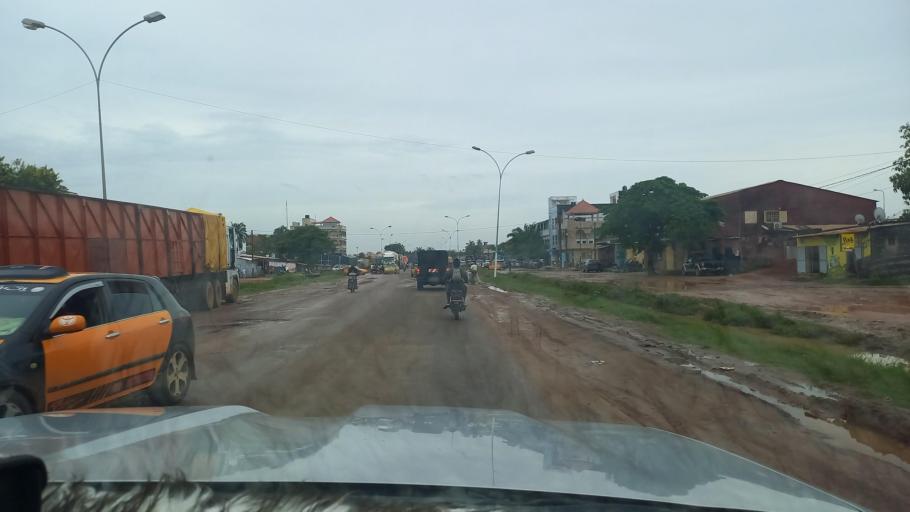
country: SN
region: Ziguinchor
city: Ziguinchor
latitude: 12.5774
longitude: -16.2675
